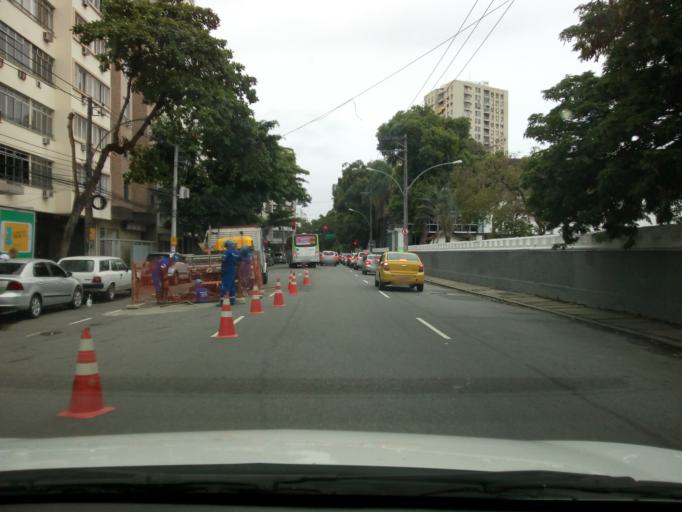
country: BR
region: Rio de Janeiro
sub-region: Rio De Janeiro
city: Rio de Janeiro
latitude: -22.9174
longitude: -43.2294
